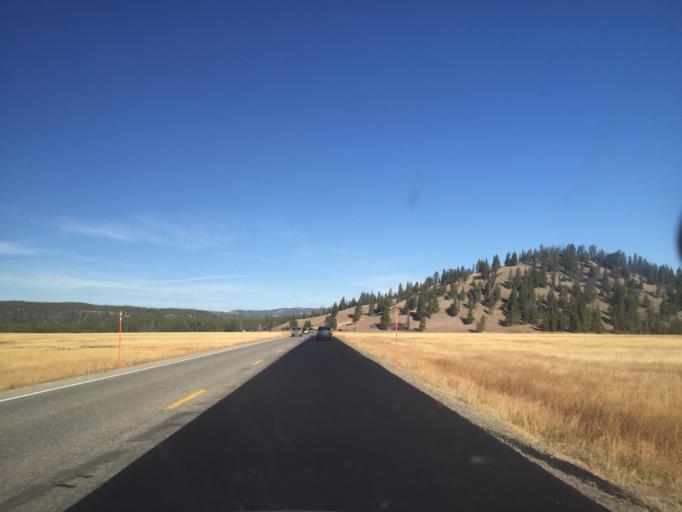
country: US
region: Montana
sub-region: Gallatin County
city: West Yellowstone
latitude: 44.5666
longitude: -110.8142
